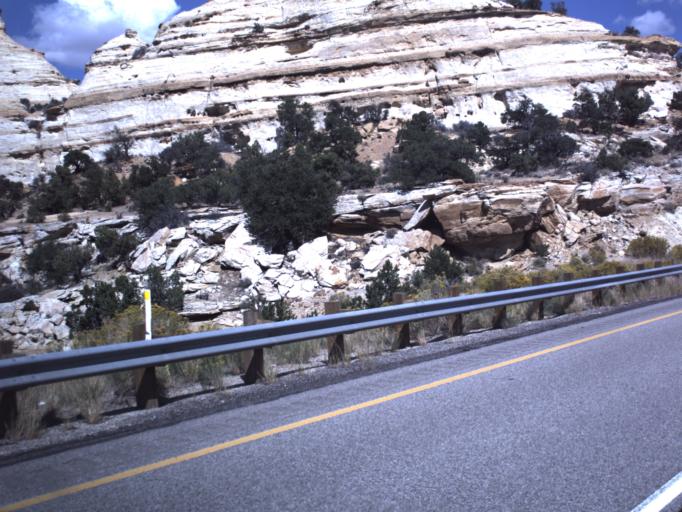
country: US
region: Utah
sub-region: Emery County
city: Ferron
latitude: 38.8525
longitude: -110.8776
